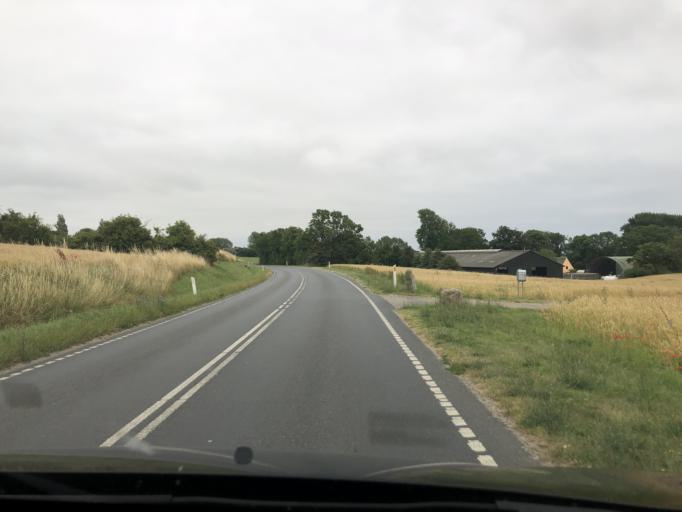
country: DK
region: South Denmark
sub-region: AEro Kommune
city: AEroskobing
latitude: 54.9068
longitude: 10.2923
